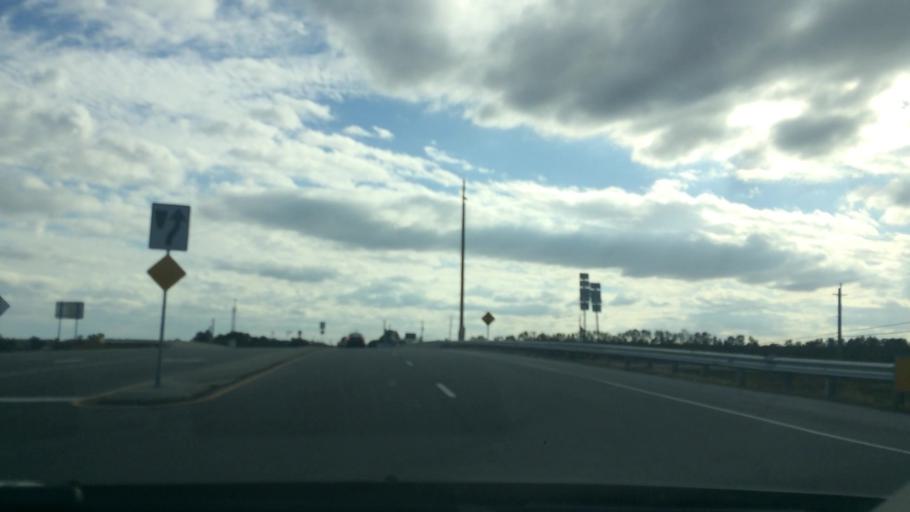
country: US
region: North Carolina
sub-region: Wayne County
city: Elroy
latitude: 35.4131
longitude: -77.8971
